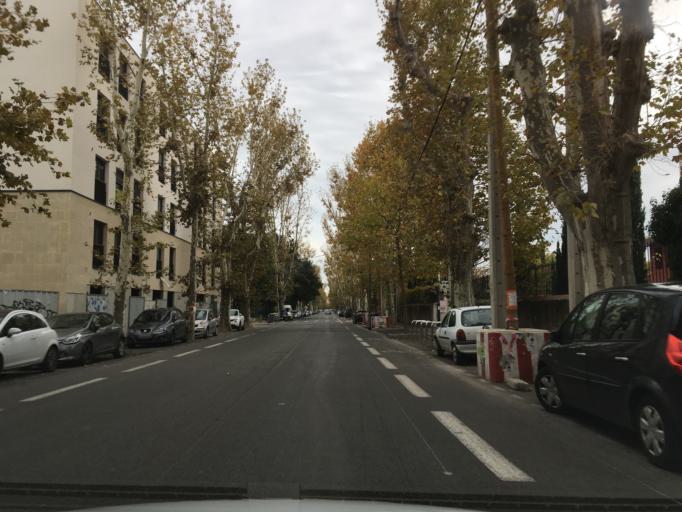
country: FR
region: Languedoc-Roussillon
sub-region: Departement de l'Herault
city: Castelnau-le-Lez
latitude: 43.6235
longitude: 3.8886
